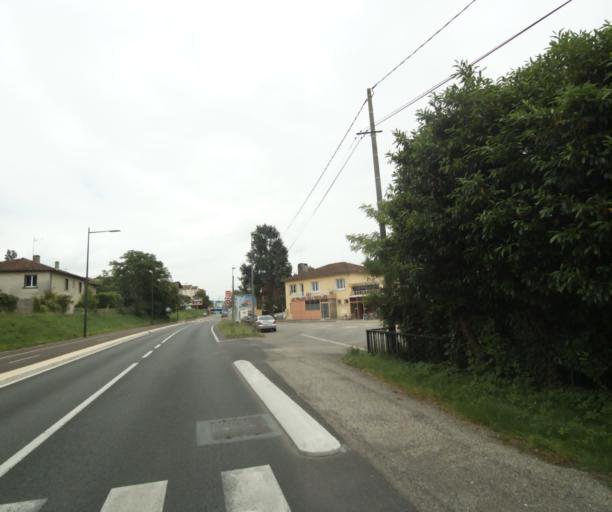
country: FR
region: Midi-Pyrenees
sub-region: Departement du Tarn-et-Garonne
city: Montauban
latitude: 44.0035
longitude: 1.3646
